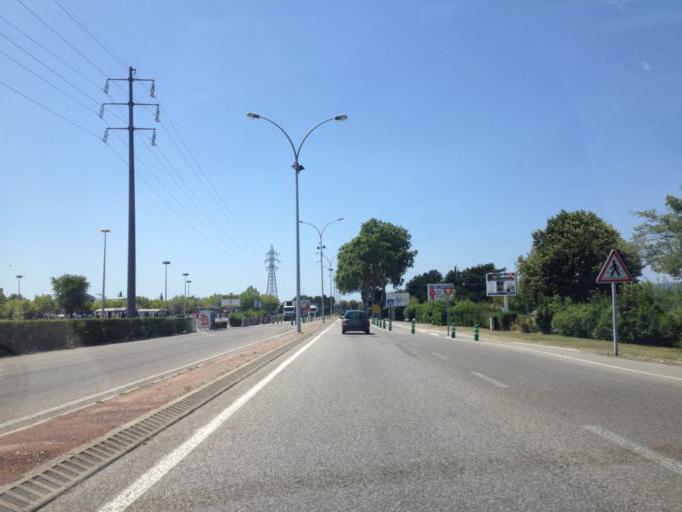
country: FR
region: Rhone-Alpes
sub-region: Departement de la Drome
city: Bourg-les-Valence
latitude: 44.9428
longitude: 4.9187
